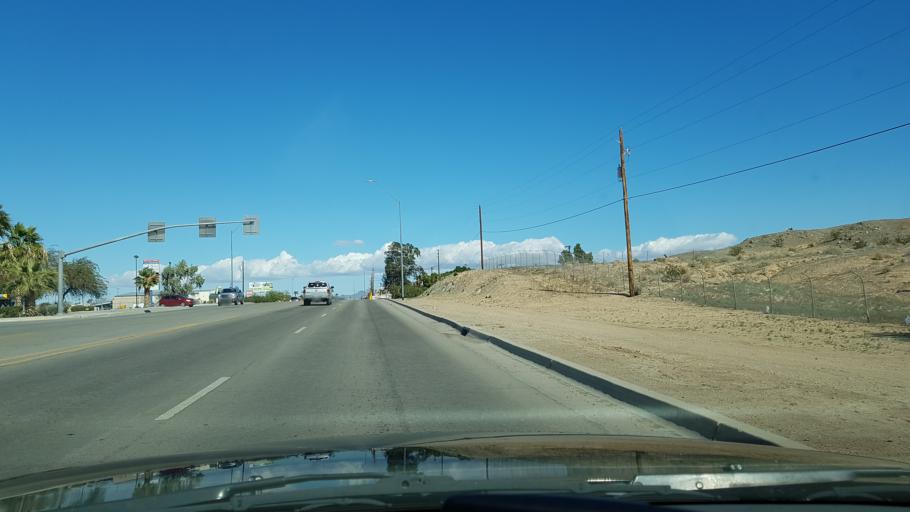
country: US
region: Arizona
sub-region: Yuma County
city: Yuma
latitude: 32.6702
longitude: -114.5986
